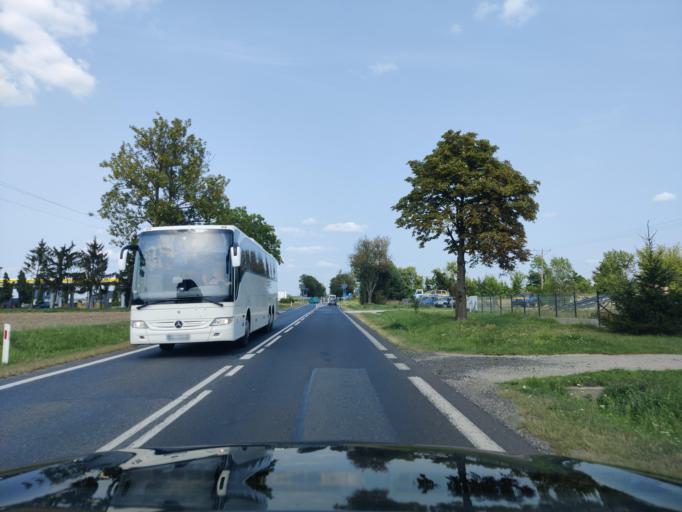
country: PL
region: Masovian Voivodeship
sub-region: Powiat pultuski
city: Pultusk
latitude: 52.7430
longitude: 21.0971
